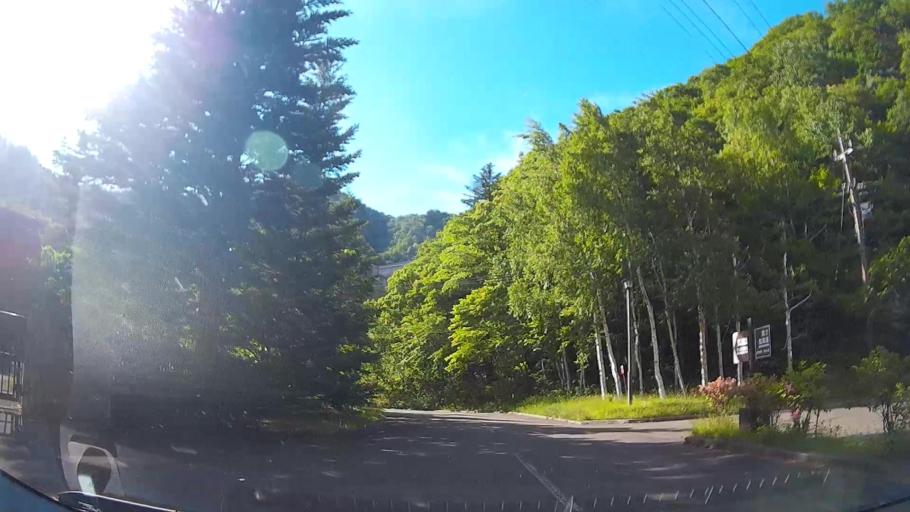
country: JP
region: Hokkaido
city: Sapporo
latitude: 42.9823
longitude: 141.1583
